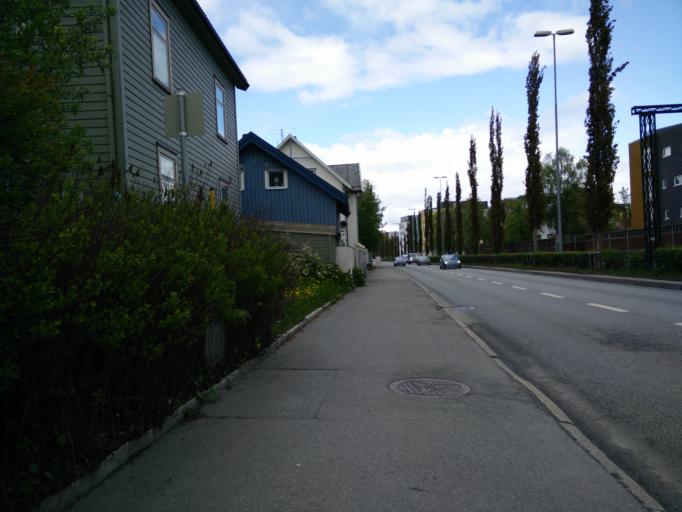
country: NO
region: Sor-Trondelag
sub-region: Trondheim
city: Trondheim
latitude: 63.4095
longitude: 10.3987
